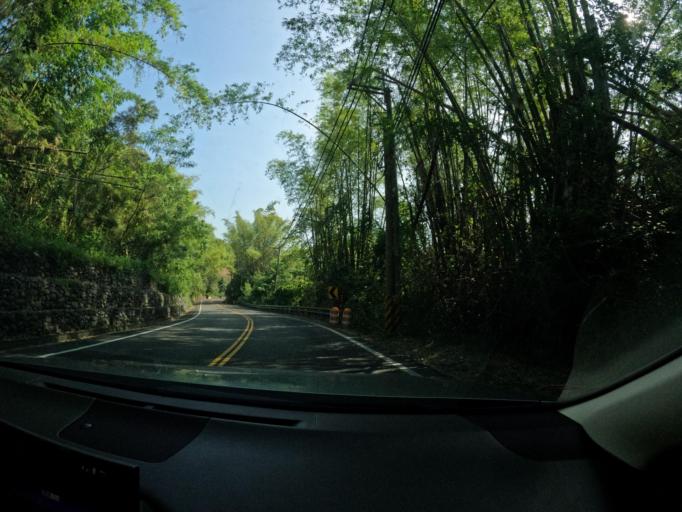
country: TW
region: Taiwan
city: Yujing
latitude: 23.0617
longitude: 120.5623
